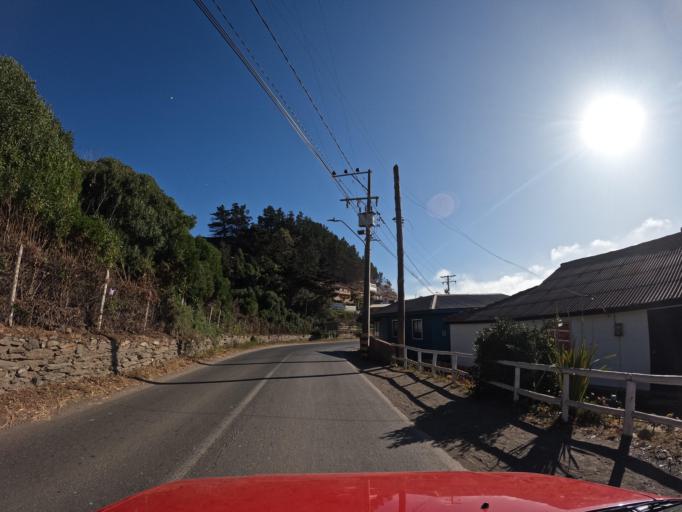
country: CL
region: Maule
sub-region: Provincia de Talca
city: Constitucion
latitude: -34.8863
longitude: -72.1685
